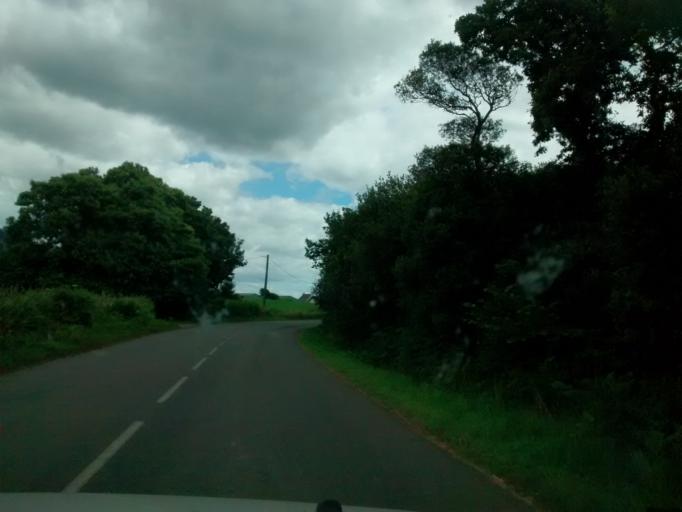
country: FR
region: Brittany
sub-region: Departement du Finistere
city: Plouneventer
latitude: 48.5466
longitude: -4.1957
